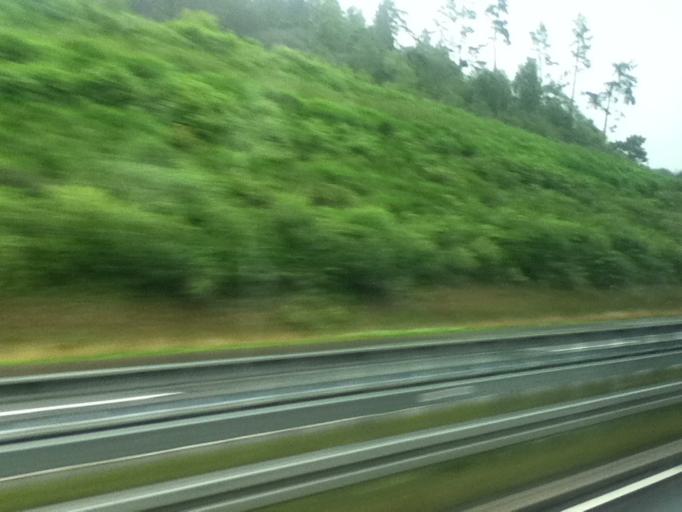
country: DE
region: North Rhine-Westphalia
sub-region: Regierungsbezirk Arnsberg
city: Wenden
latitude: 50.9947
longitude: 7.8774
